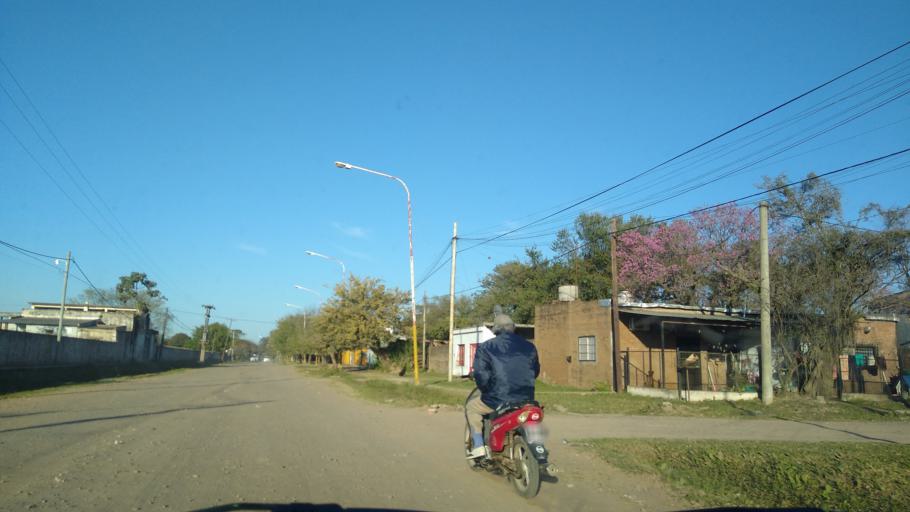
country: AR
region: Chaco
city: Barranqueras
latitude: -27.4792
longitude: -58.9465
